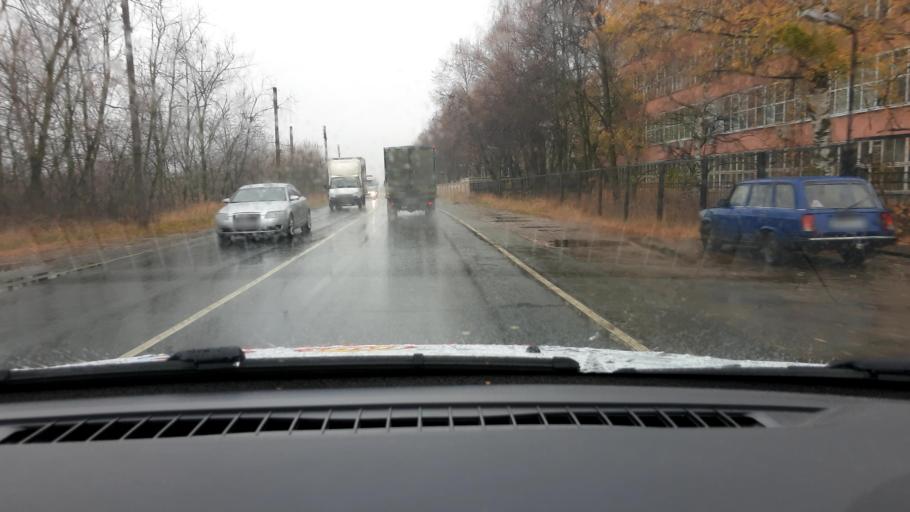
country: RU
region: Nizjnij Novgorod
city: Babino
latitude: 56.2586
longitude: 43.6412
